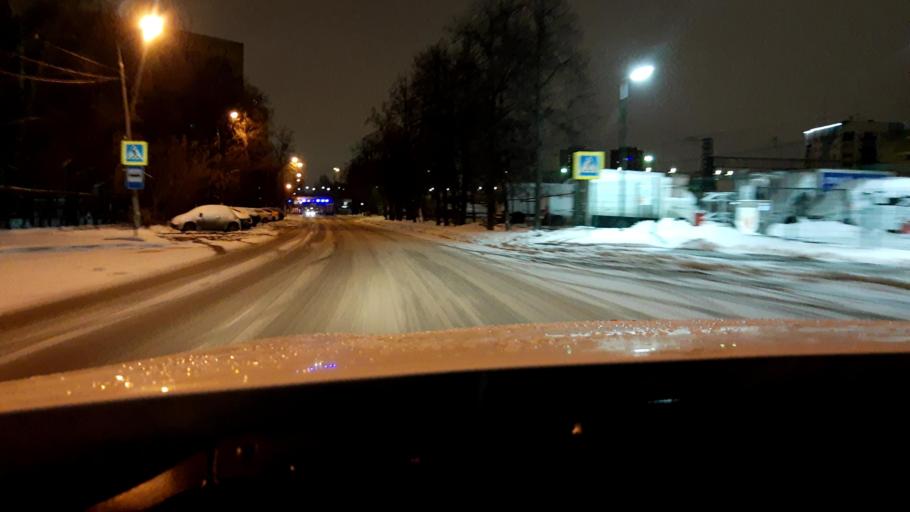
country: RU
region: Moscow
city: Khimki
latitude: 55.8982
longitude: 37.4444
